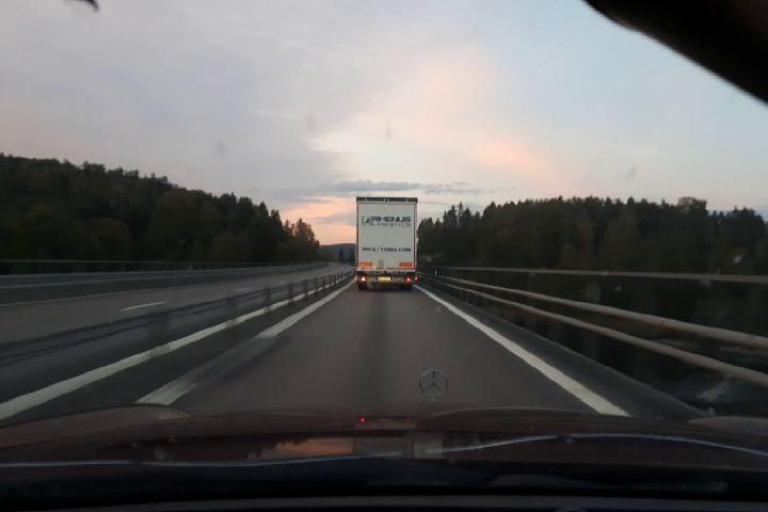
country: SE
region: Vaesternorrland
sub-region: Haernoesands Kommun
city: Haernoesand
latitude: 62.8217
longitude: 17.9702
